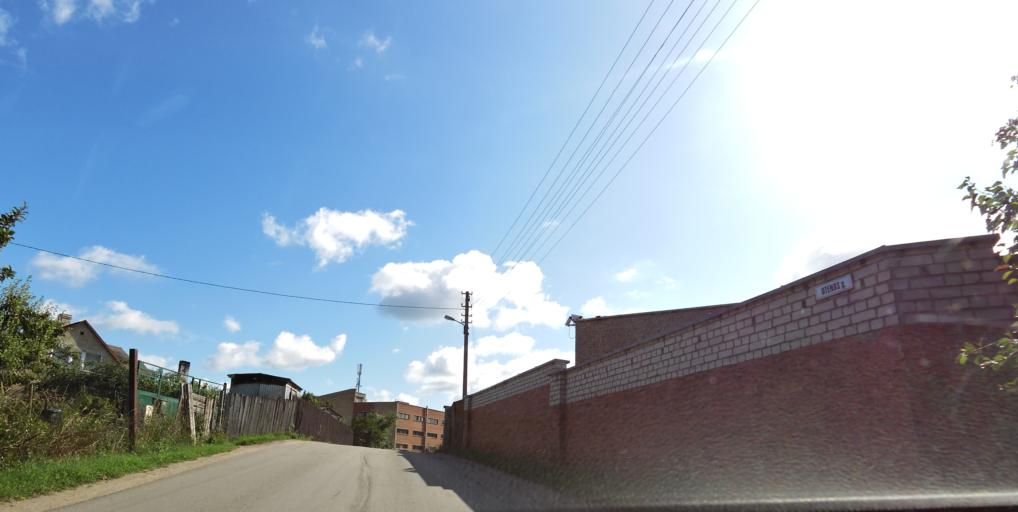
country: LT
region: Vilnius County
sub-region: Vilnius
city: Vilnius
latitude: 54.7062
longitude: 25.2726
